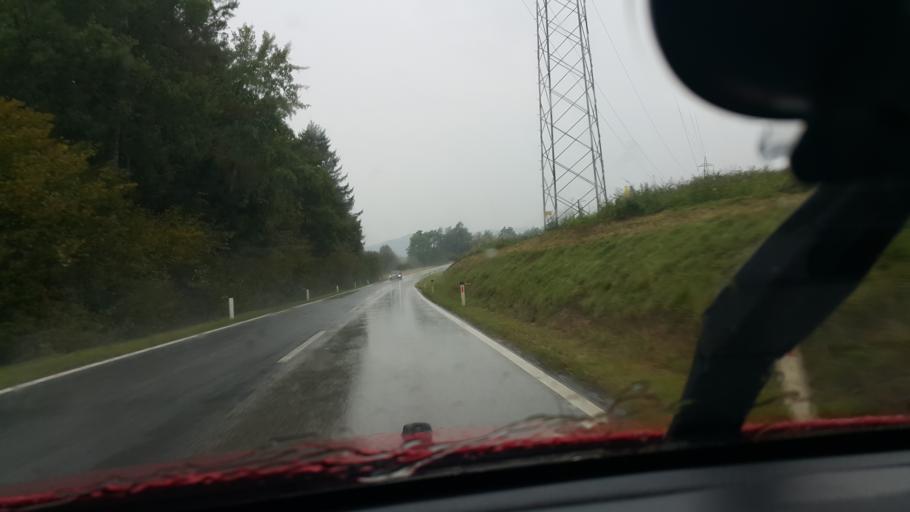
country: AT
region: Carinthia
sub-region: Politischer Bezirk Volkermarkt
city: Ruden
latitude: 46.6466
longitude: 14.8049
